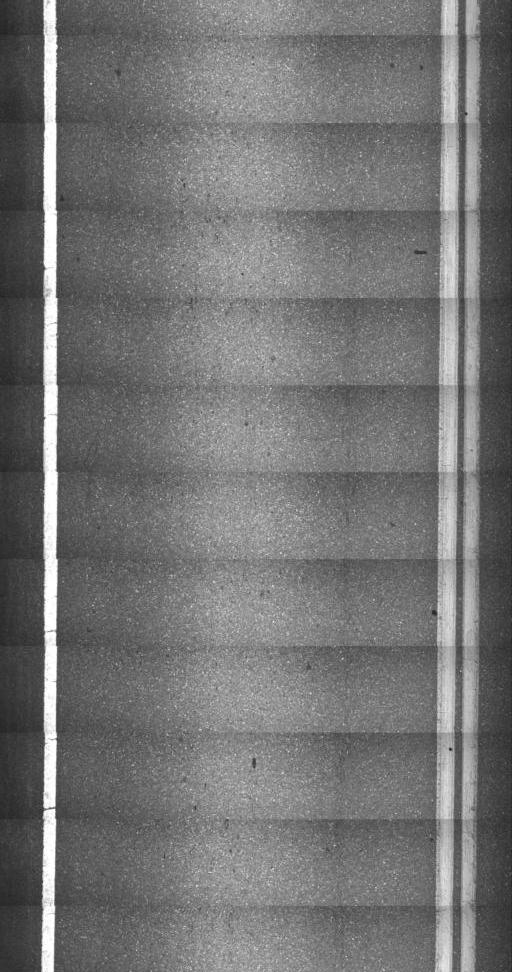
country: US
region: Vermont
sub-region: Windham County
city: Brattleboro
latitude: 42.8602
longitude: -72.5647
